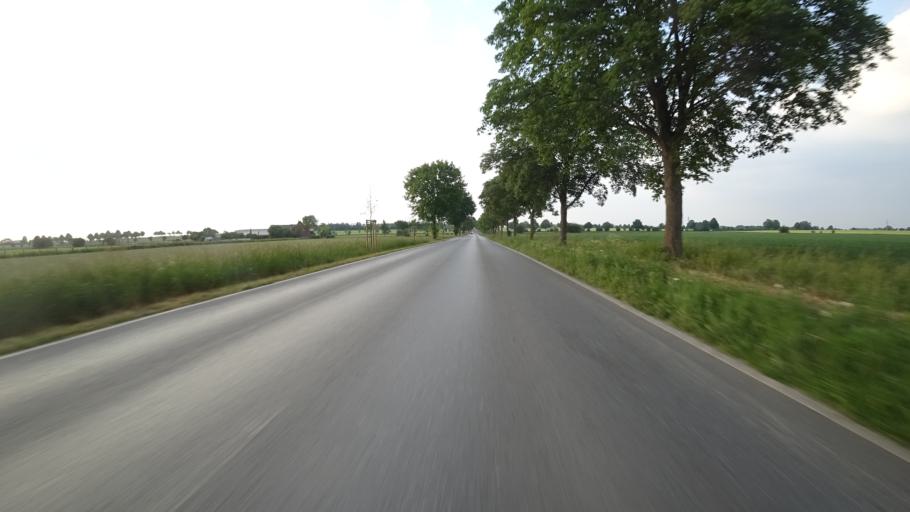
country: DE
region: North Rhine-Westphalia
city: Erwitte
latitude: 51.6395
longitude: 8.3572
